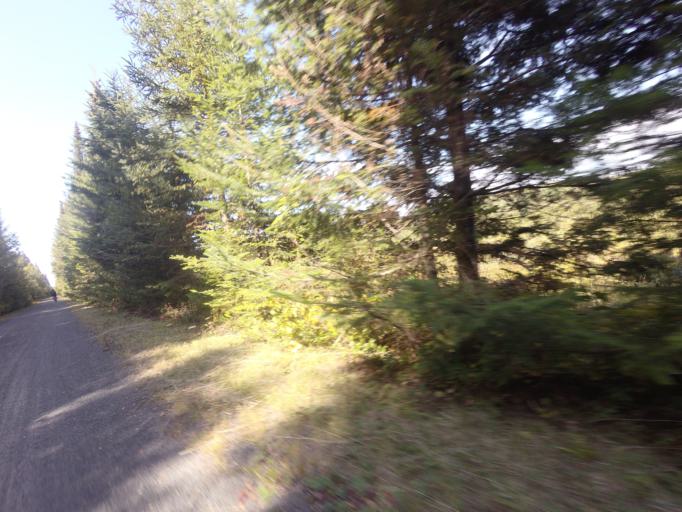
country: CA
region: Quebec
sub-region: Laurentides
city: Sainte-Agathe-des-Monts
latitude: 46.0950
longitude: -74.3519
